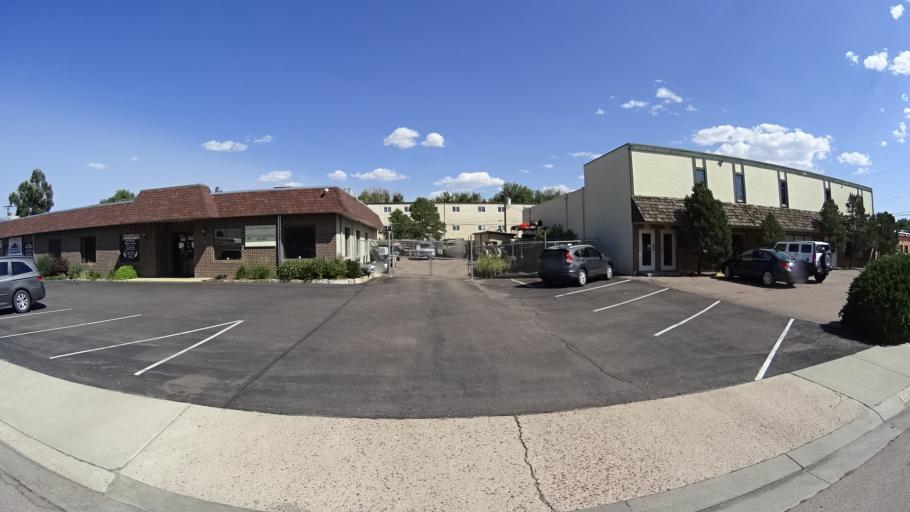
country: US
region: Colorado
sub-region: El Paso County
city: Colorado Springs
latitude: 38.8729
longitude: -104.8112
